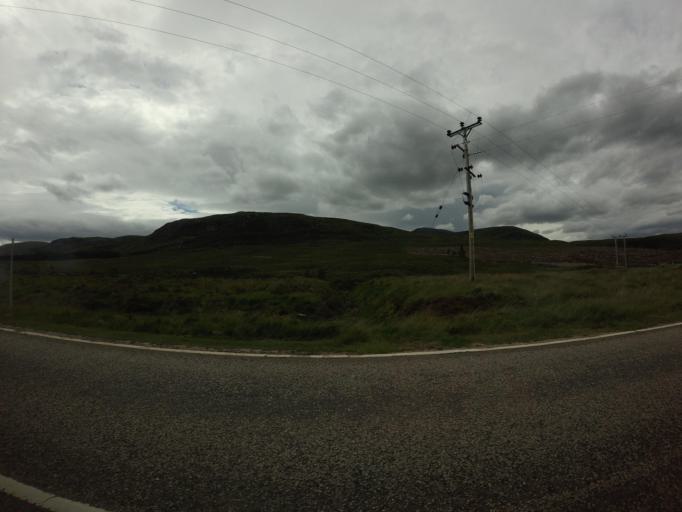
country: GB
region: Scotland
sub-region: Highland
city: Ullapool
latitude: 57.7521
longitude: -5.0054
